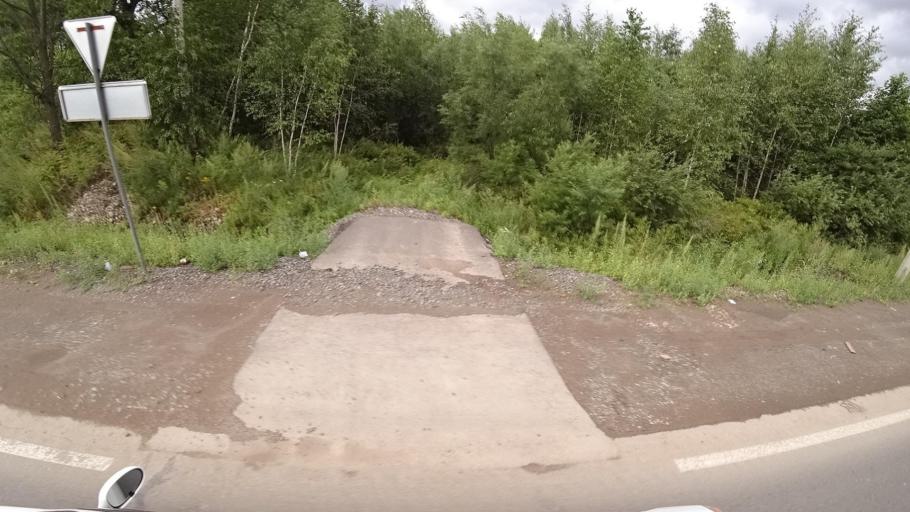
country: RU
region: Khabarovsk Krai
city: Solnechnyy
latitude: 50.5873
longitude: 137.0274
